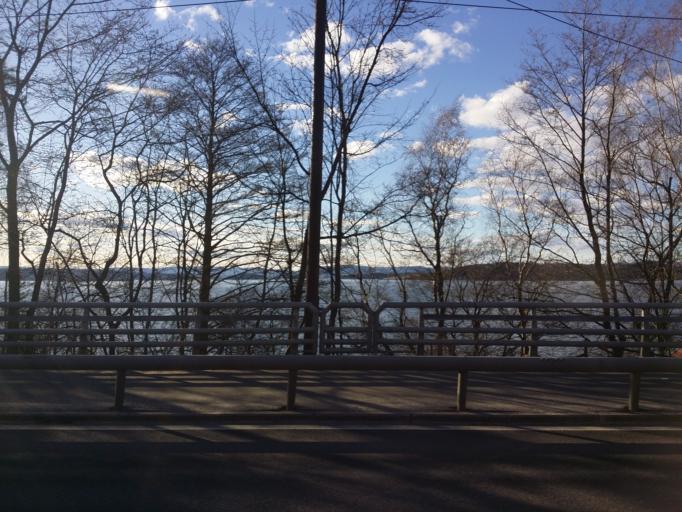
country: NO
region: Akershus
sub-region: Oppegard
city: Kolbotn
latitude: 59.8494
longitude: 10.7813
